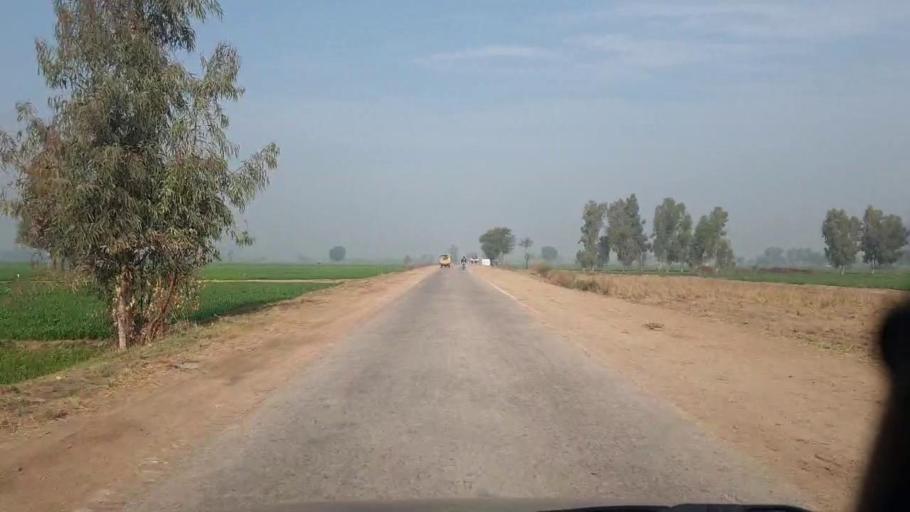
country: PK
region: Sindh
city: Shahdadpur
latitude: 25.9577
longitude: 68.5879
